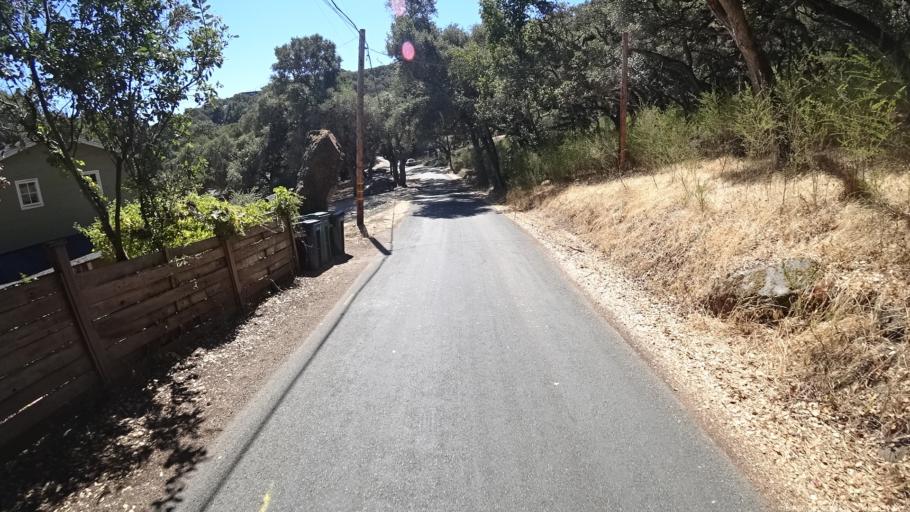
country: US
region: California
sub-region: Monterey County
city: Carmel Valley Village
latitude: 36.4680
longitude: -121.7307
